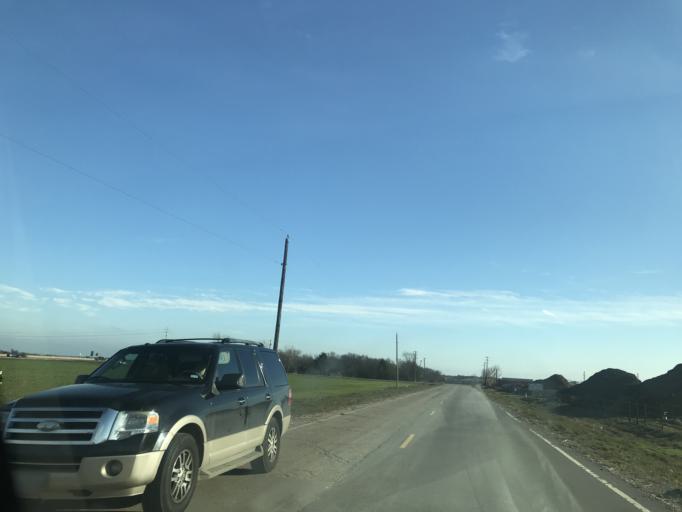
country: US
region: Texas
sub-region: Dallas County
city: Wilmer
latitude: 32.5677
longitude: -96.6703
